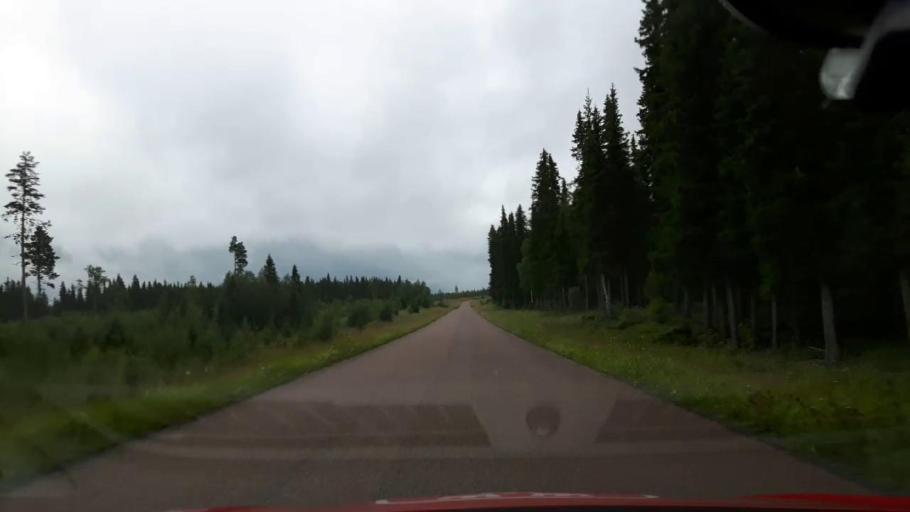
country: SE
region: Jaemtland
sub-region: Krokoms Kommun
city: Valla
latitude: 63.3788
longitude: 13.7584
